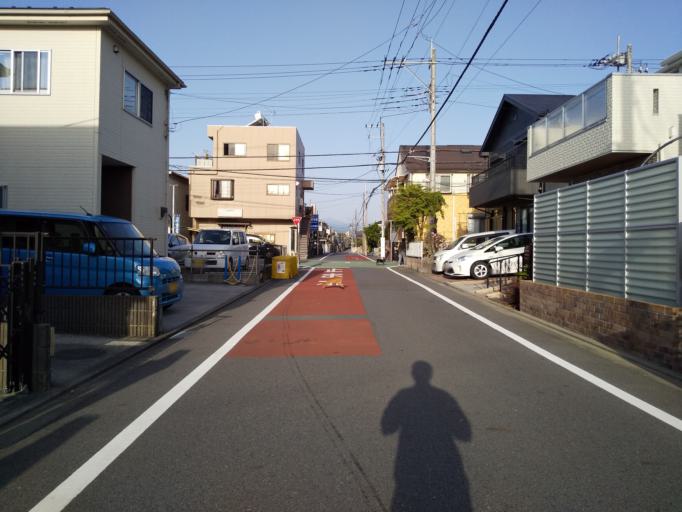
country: JP
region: Kanagawa
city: Zama
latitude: 35.5605
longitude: 139.3782
